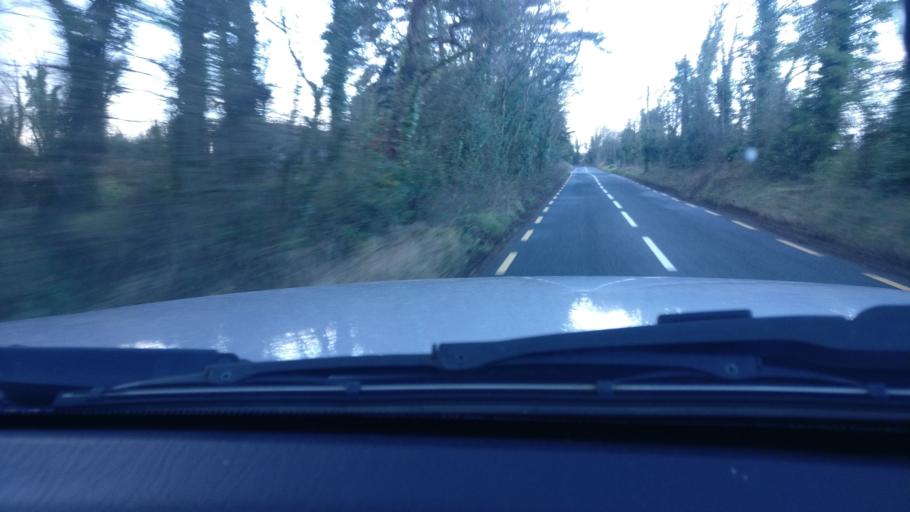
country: IE
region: Connaught
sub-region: County Galway
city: Loughrea
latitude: 53.2237
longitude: -8.3874
